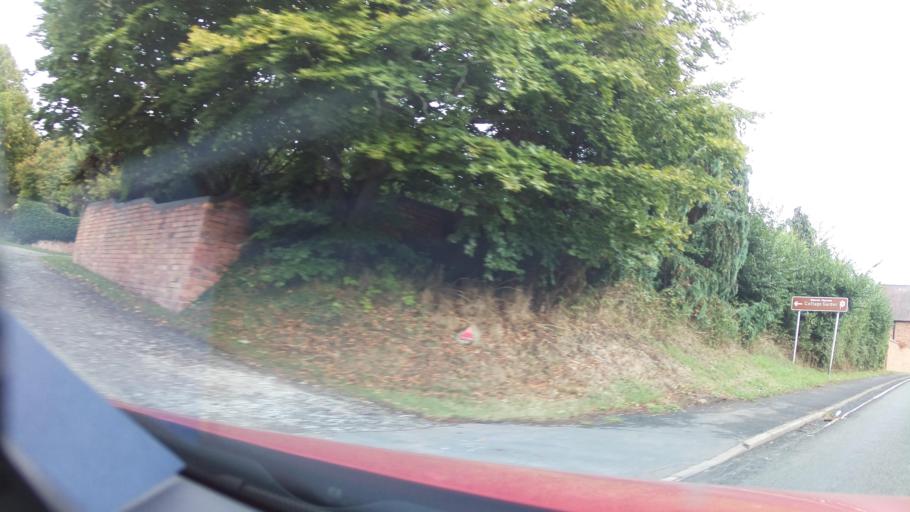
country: GB
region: England
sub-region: Worcestershire
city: Kidderminster
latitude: 52.3730
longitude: -2.2063
